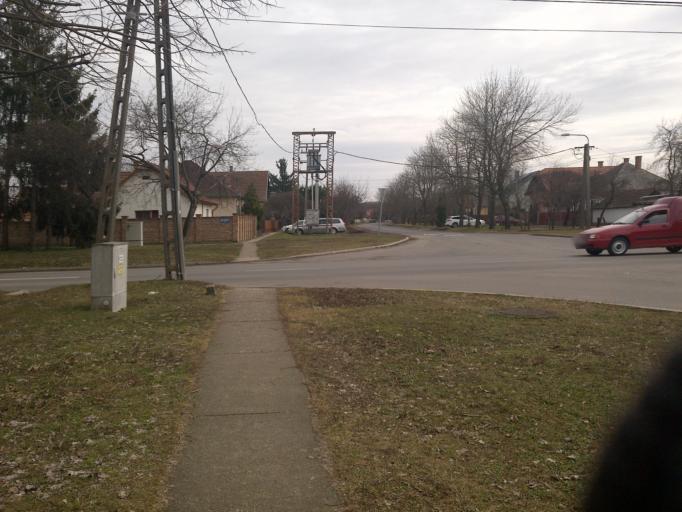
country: HU
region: Hajdu-Bihar
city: Hajduszoboszlo
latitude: 47.4386
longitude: 21.4088
